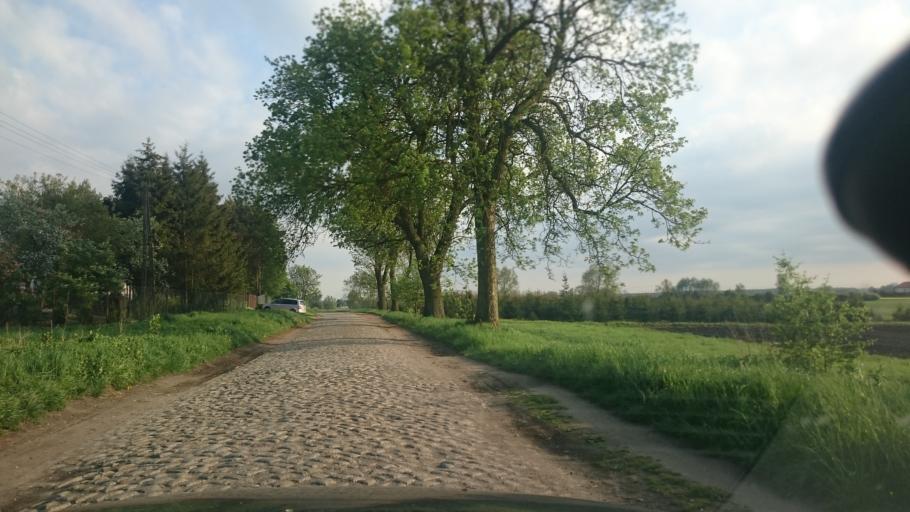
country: PL
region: Kujawsko-Pomorskie
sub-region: Grudziadz
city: Grudziadz
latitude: 53.4730
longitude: 18.8140
